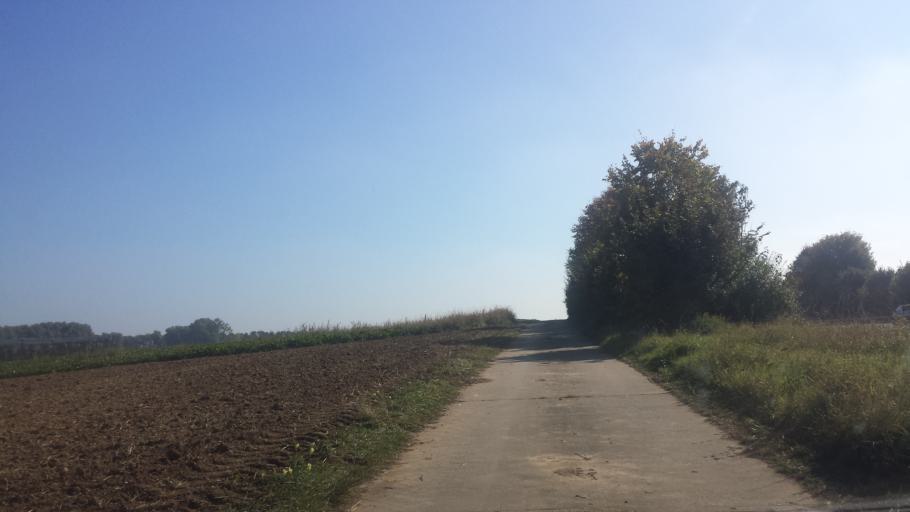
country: DE
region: Rheinland-Pfalz
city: Insheim
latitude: 49.1487
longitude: 8.1579
